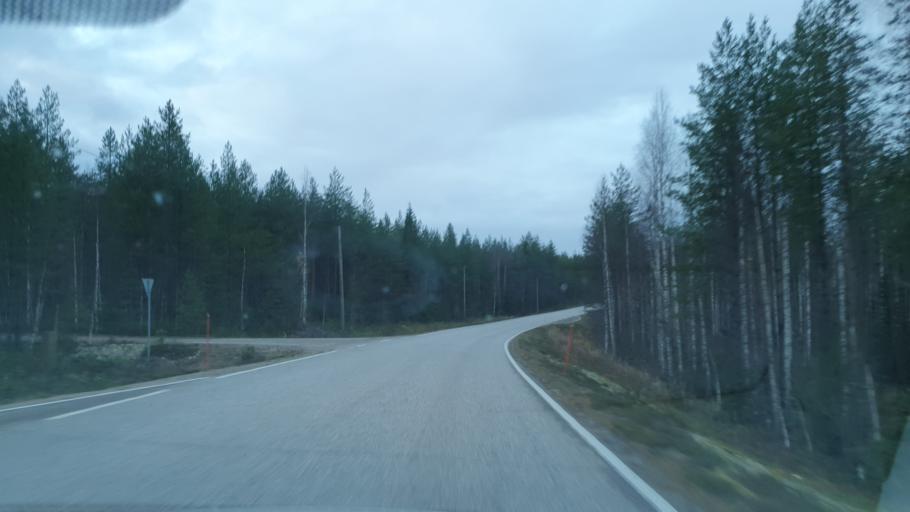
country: FI
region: Kainuu
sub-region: Kajaani
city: Ristijaervi
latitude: 64.4314
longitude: 28.3697
